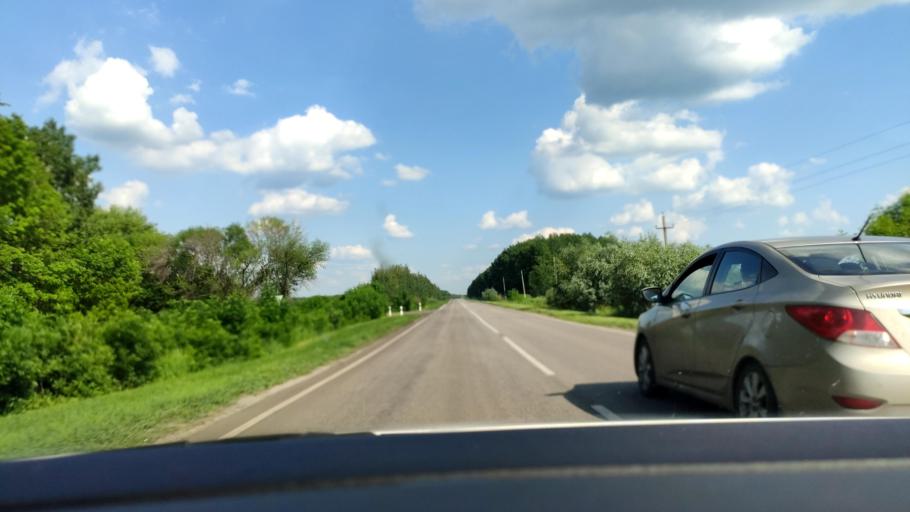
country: RU
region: Voronezj
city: Panino
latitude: 51.6625
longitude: 39.9807
